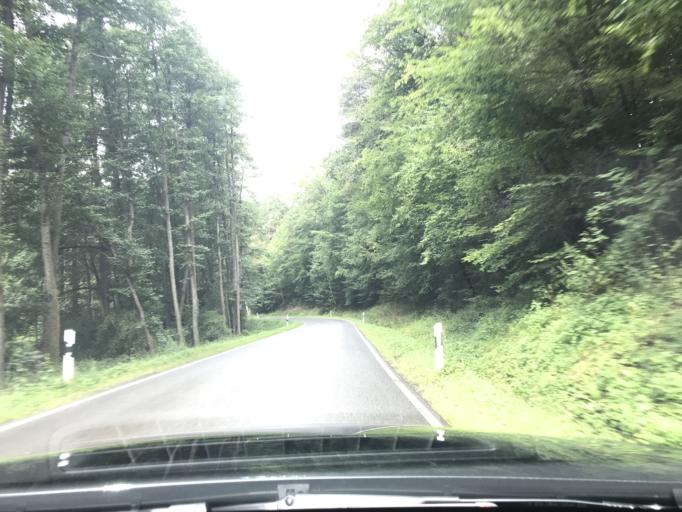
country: DE
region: Bavaria
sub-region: Regierungsbezirk Unterfranken
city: Breitbrunn
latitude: 50.0312
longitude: 10.6747
